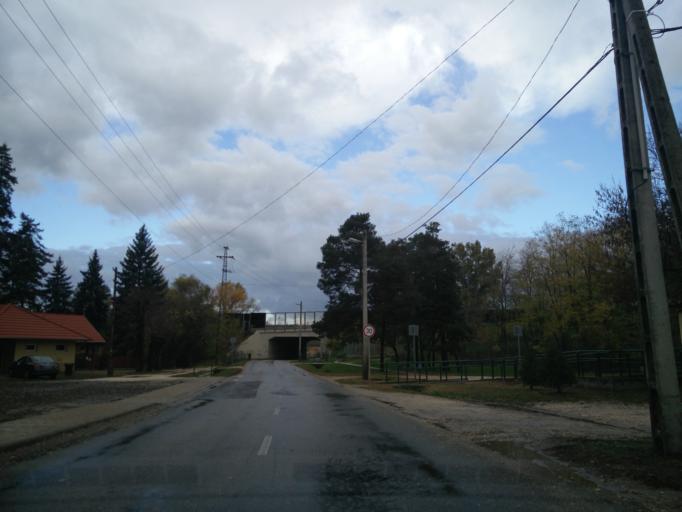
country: HU
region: Pest
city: Mogyorod
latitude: 47.5924
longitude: 19.2406
